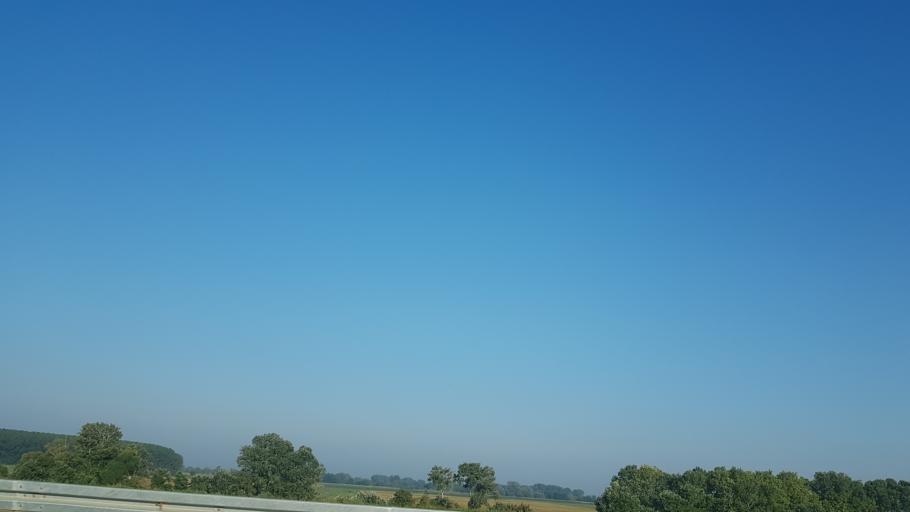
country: TR
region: Bursa
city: Karacabey
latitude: 40.1527
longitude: 28.3103
